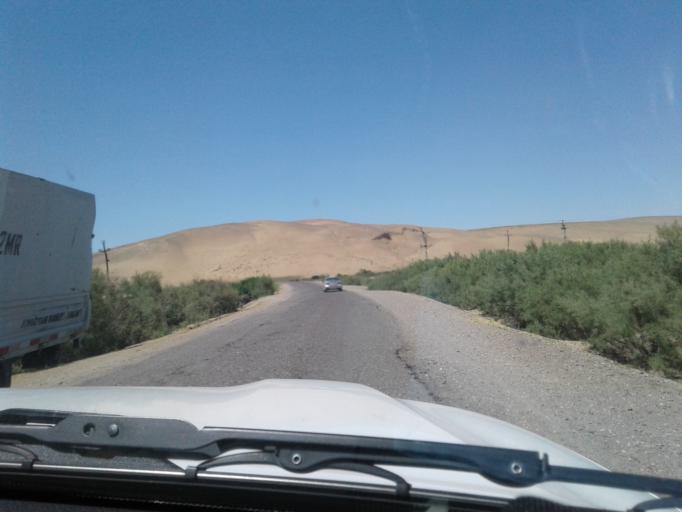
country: AF
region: Badghis
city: Bala Murghab
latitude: 35.9621
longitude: 62.9077
